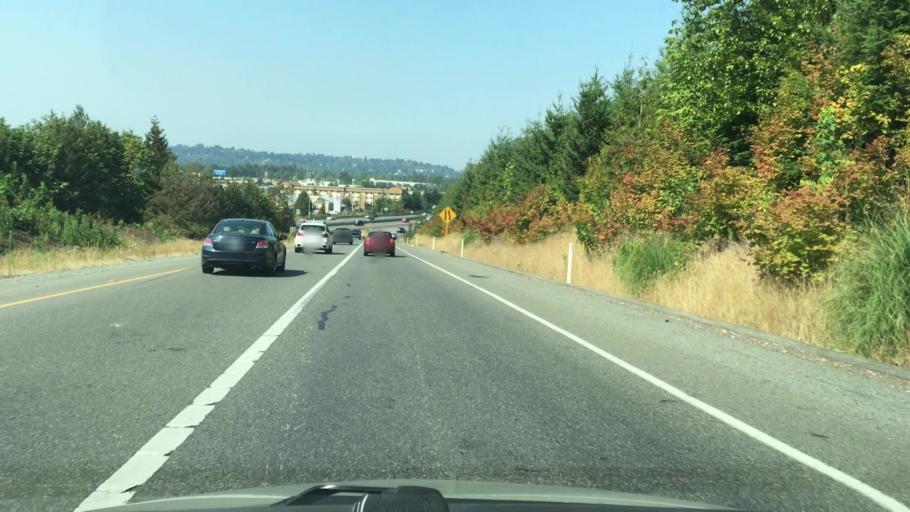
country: US
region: Washington
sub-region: King County
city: Renton
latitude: 47.4417
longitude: -122.2160
